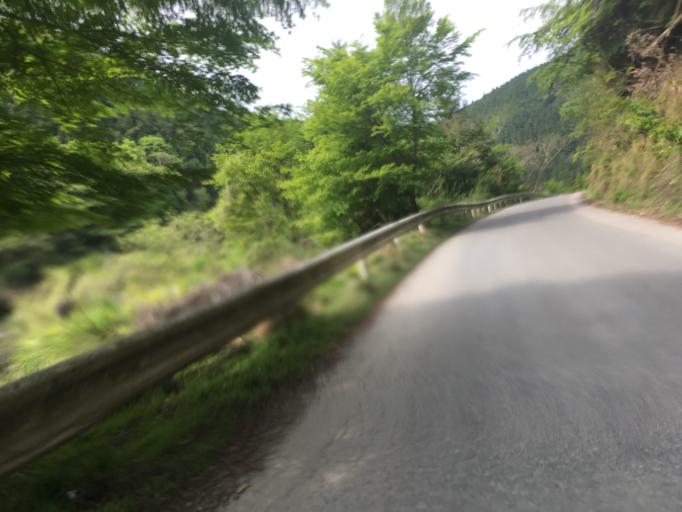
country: JP
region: Kyoto
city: Kameoka
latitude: 35.1359
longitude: 135.5758
